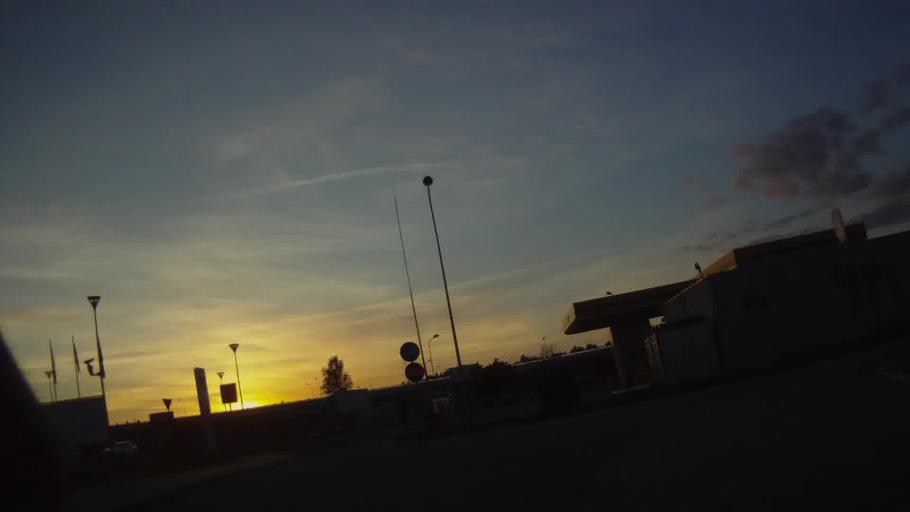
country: LV
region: Riga
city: Bergi
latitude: 57.0019
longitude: 24.2857
